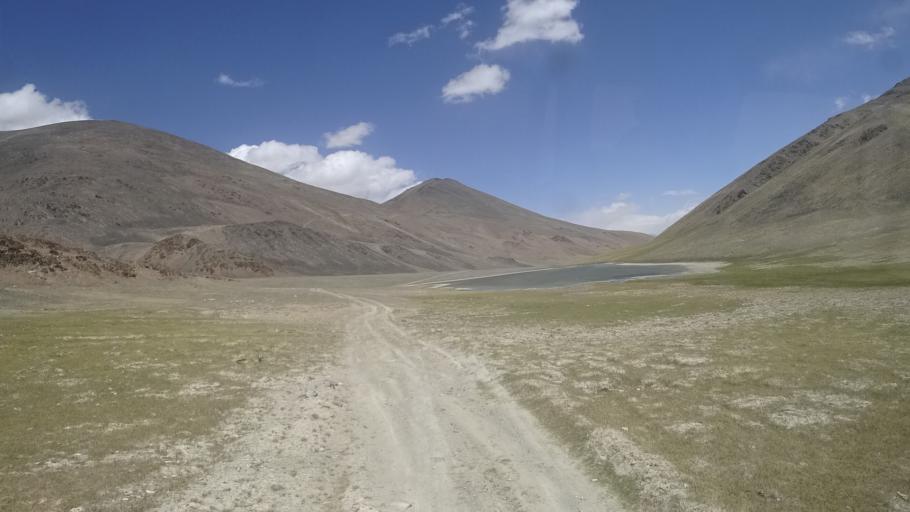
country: TJ
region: Gorno-Badakhshan
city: Murghob
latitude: 37.5197
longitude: 74.0602
